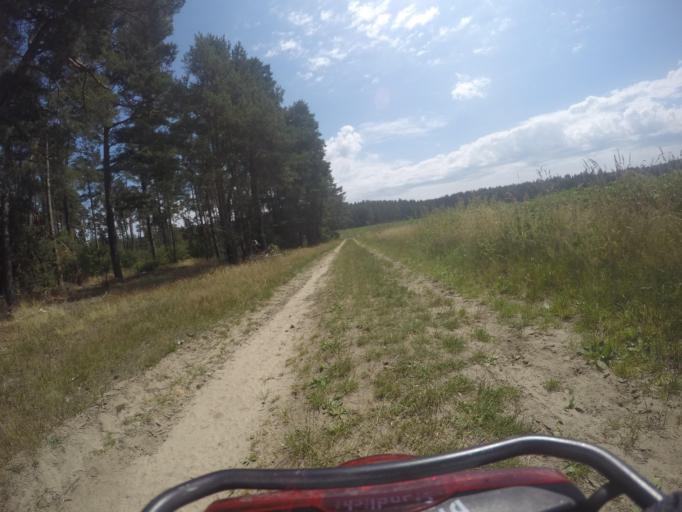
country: DE
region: Lower Saxony
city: Dahlem
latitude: 53.2233
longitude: 10.7296
